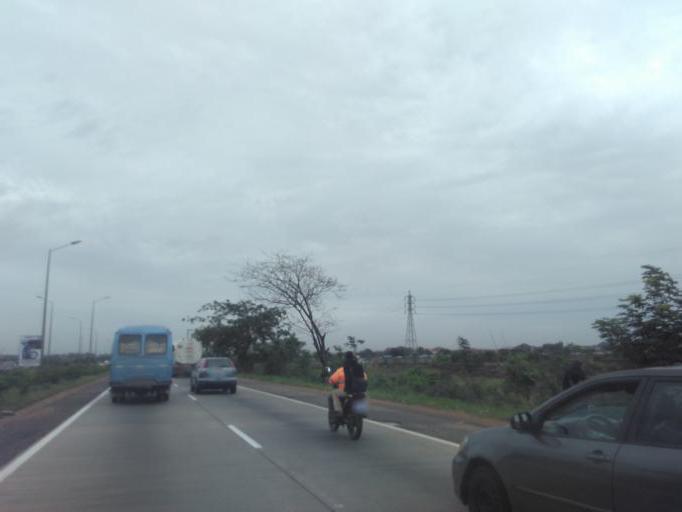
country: GH
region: Greater Accra
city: Nungua
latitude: 5.6553
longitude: -0.0924
